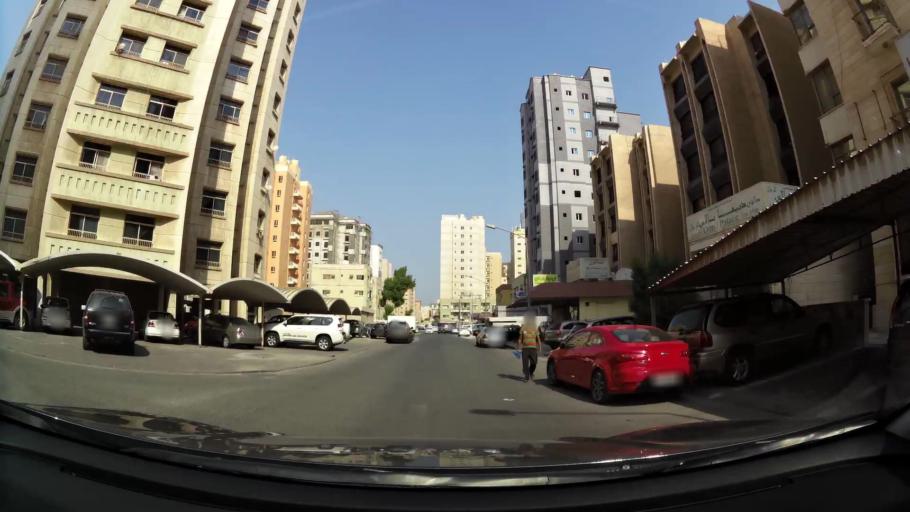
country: KW
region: Muhafazat Hawalli
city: Ar Rumaythiyah
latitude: 29.3212
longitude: 48.0594
